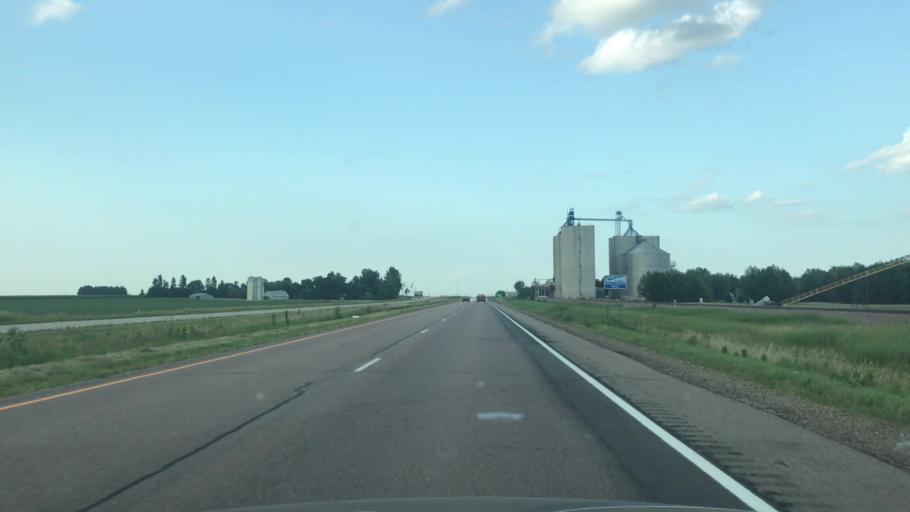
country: US
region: Minnesota
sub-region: Nobles County
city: Worthington
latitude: 43.6943
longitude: -95.4781
